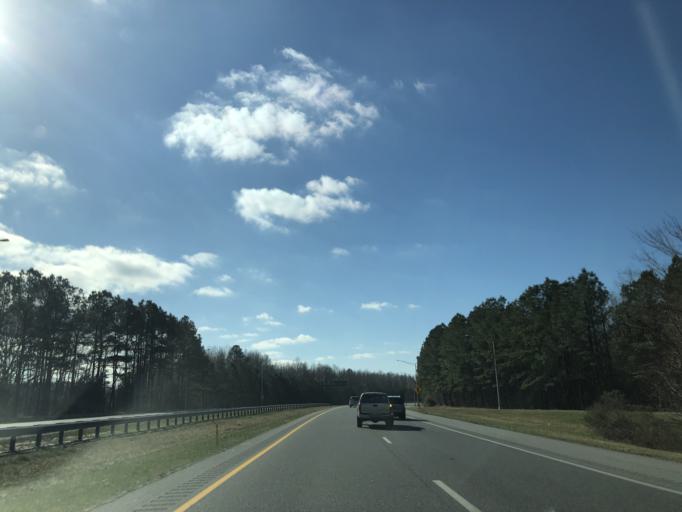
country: US
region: Maryland
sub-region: Worcester County
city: Berlin
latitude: 38.3752
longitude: -75.2065
